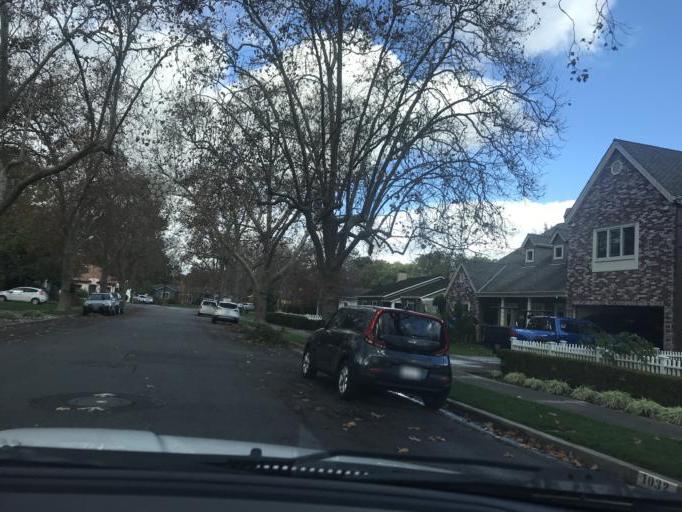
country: US
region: California
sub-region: Santa Clara County
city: Buena Vista
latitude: 37.3072
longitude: -121.9085
